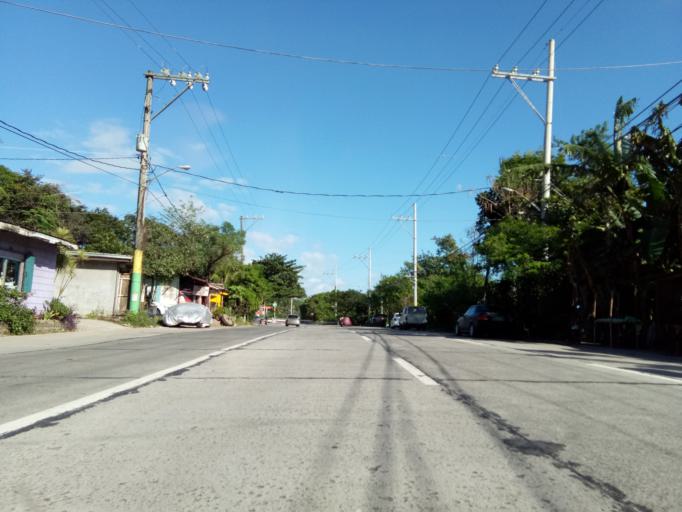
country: PH
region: Calabarzon
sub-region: Province of Cavite
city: Dasmarinas
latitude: 14.3497
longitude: 120.9696
